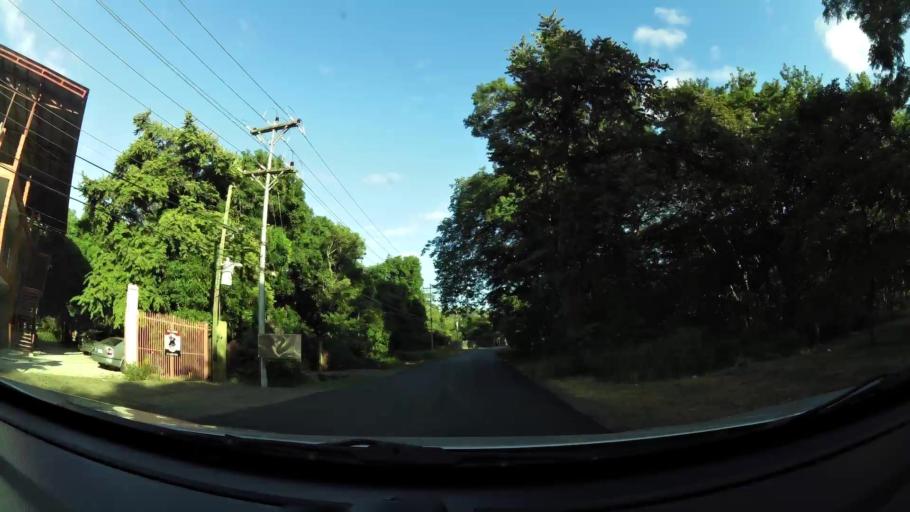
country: CR
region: Guanacaste
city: Sardinal
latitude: 10.5367
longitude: -85.6857
